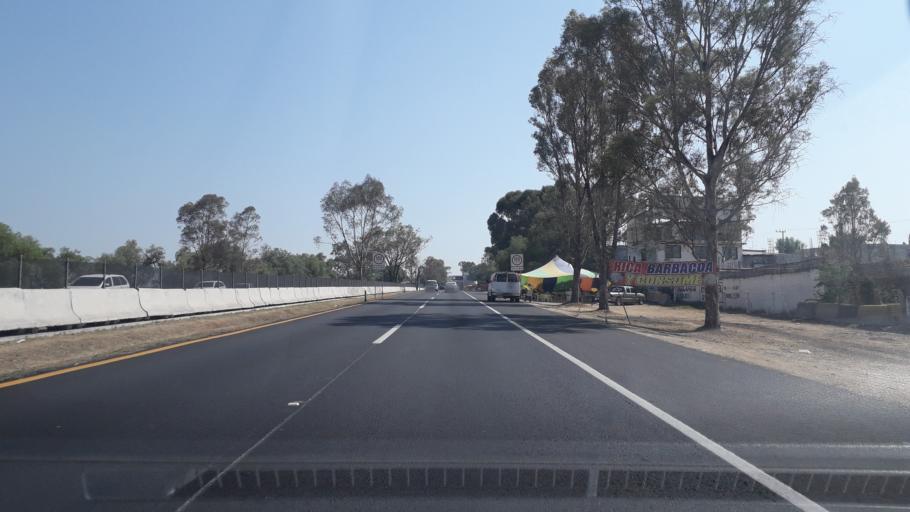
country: MX
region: Mexico
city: Santo Tomas Chiconautla
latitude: 19.6507
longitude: -99.0125
